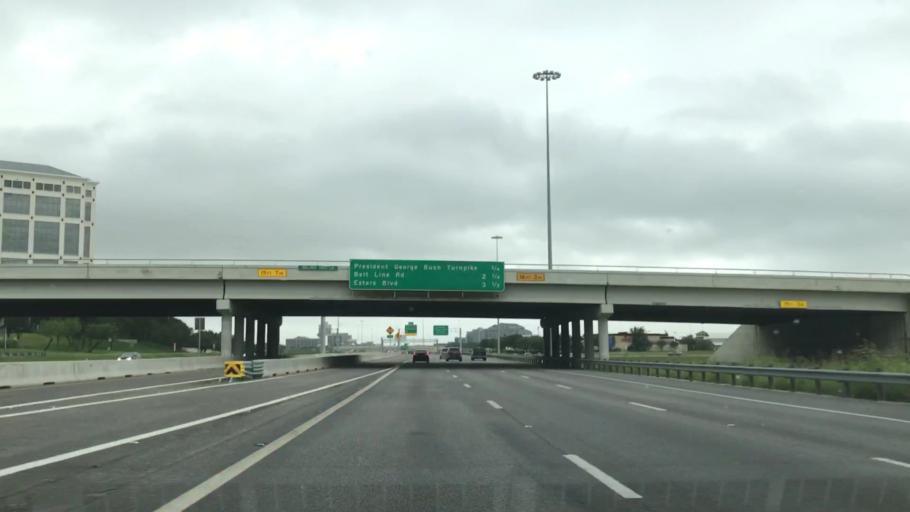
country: US
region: Texas
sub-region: Dallas County
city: Farmers Branch
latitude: 32.8865
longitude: -96.9553
